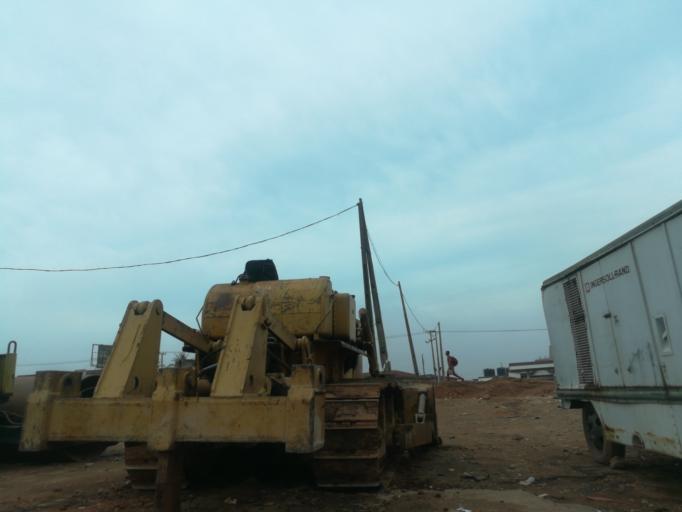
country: NG
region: Oyo
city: Ibadan
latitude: 7.3648
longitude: 3.9280
